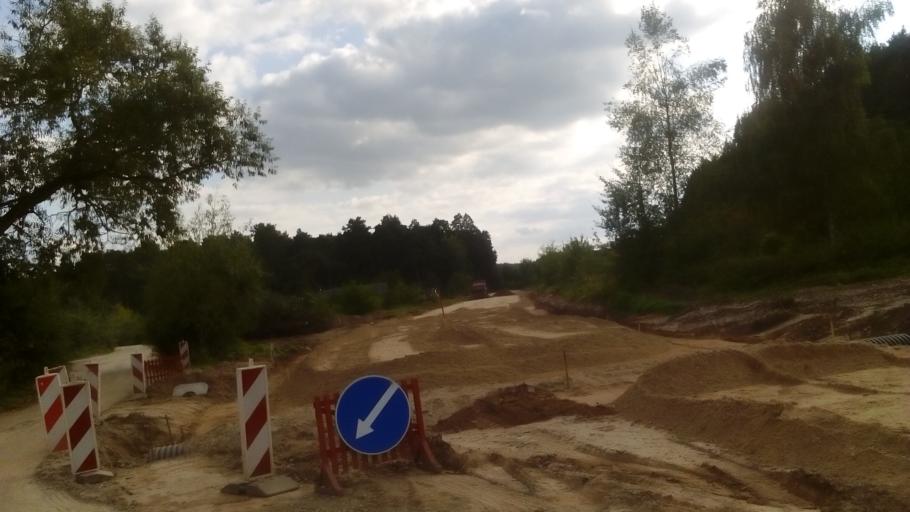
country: LT
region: Alytaus apskritis
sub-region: Alytus
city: Alytus
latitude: 54.4191
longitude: 24.0375
